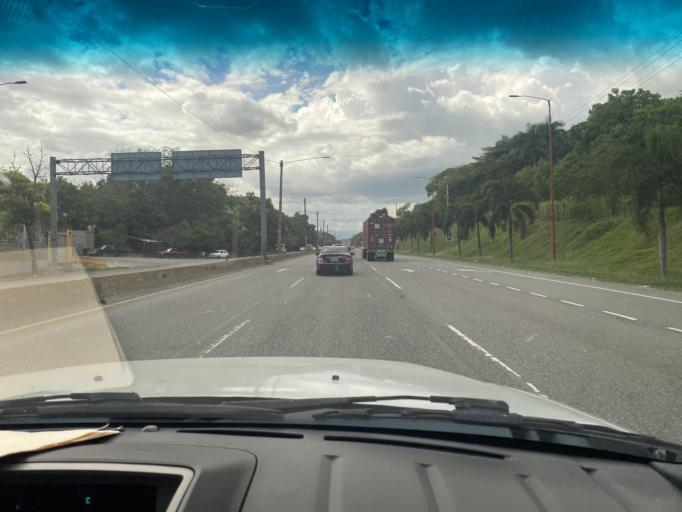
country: DO
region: Santo Domingo
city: Santo Domingo Oeste
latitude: 18.5634
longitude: -70.0722
